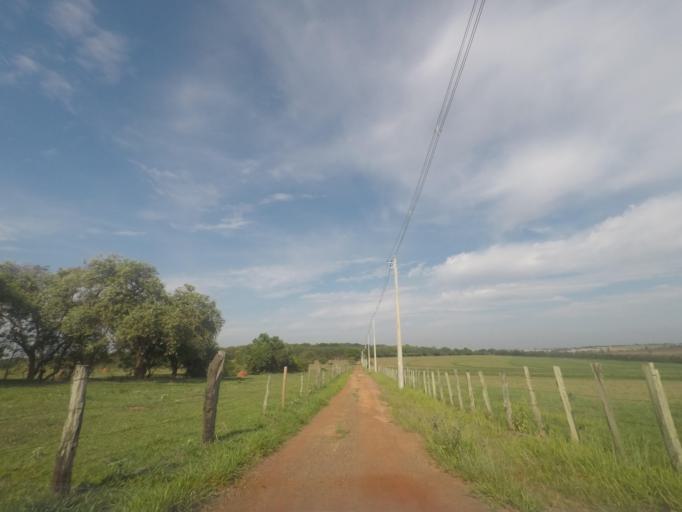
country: BR
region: Sao Paulo
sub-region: Sumare
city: Sumare
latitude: -22.7849
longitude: -47.2456
